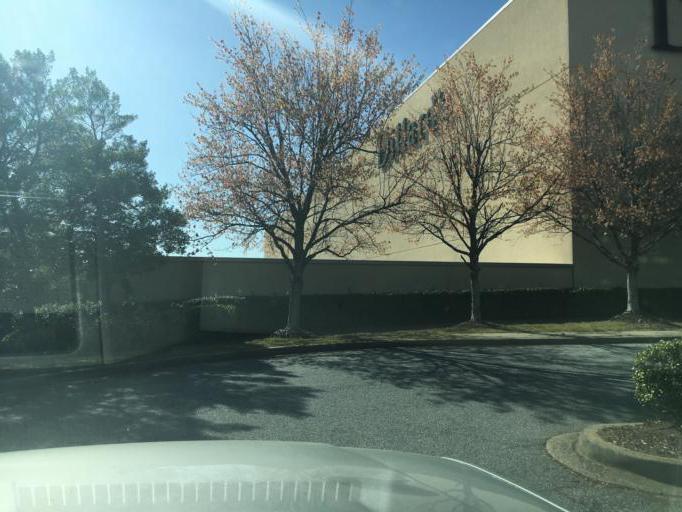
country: US
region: South Carolina
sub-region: Greenville County
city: Wade Hampton
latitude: 34.8497
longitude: -82.3303
